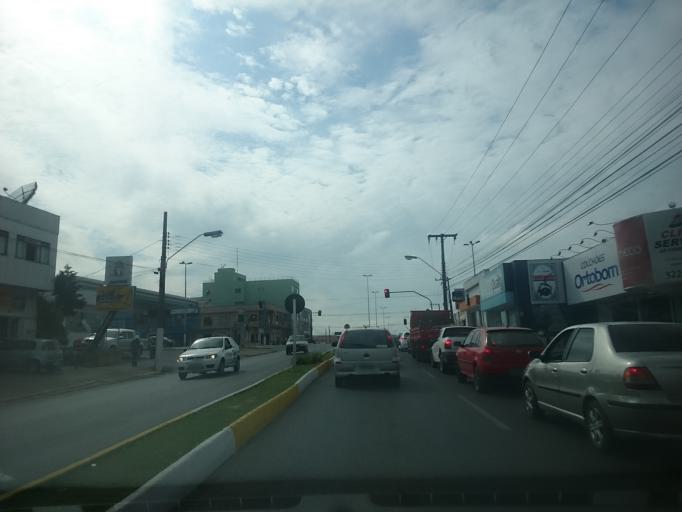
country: BR
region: Santa Catarina
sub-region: Lages
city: Lages
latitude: -27.8111
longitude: -50.3052
